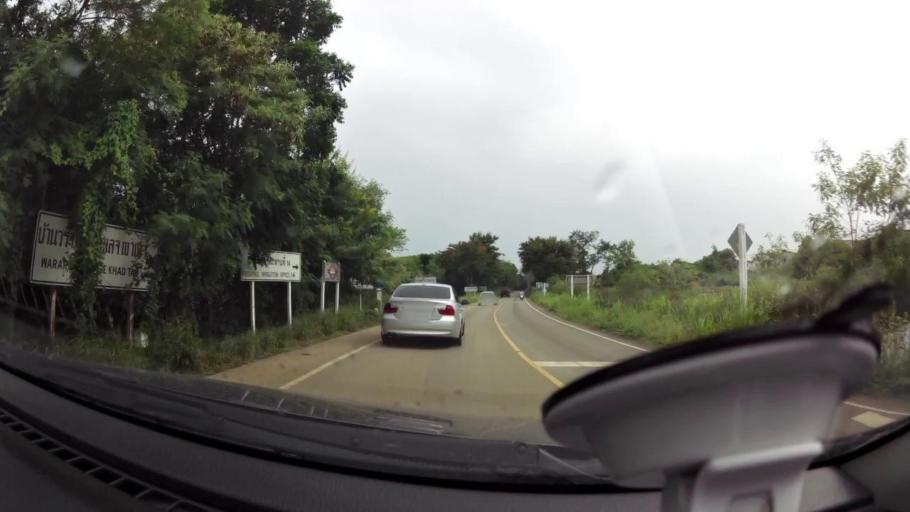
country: TH
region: Prachuap Khiri Khan
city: Pran Buri
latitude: 12.4470
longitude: 99.9633
